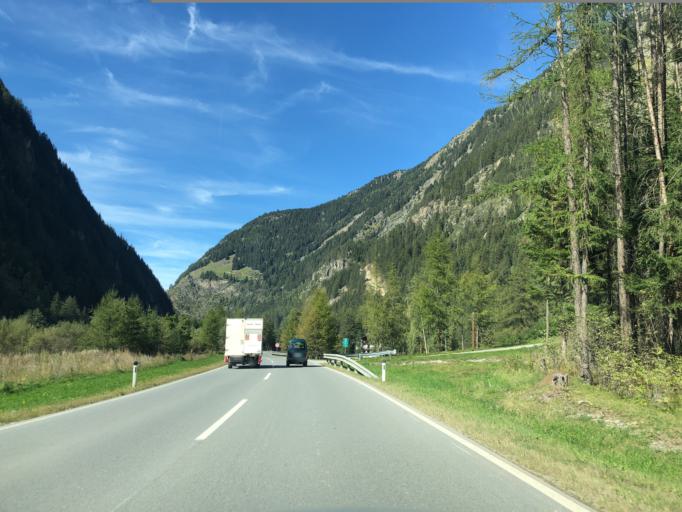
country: AT
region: Tyrol
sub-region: Politischer Bezirk Imst
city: Soelden
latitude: 47.0268
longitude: 10.9937
